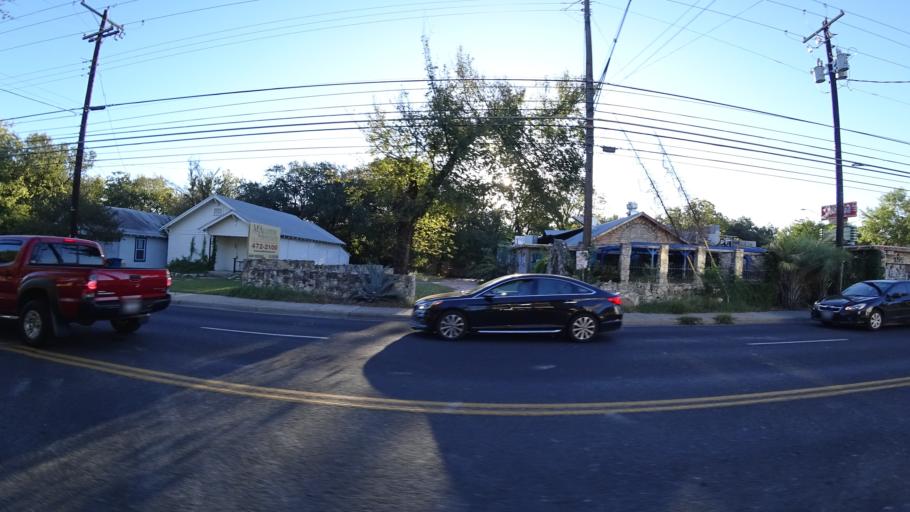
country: US
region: Texas
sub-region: Travis County
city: Austin
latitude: 30.2485
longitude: -97.7555
